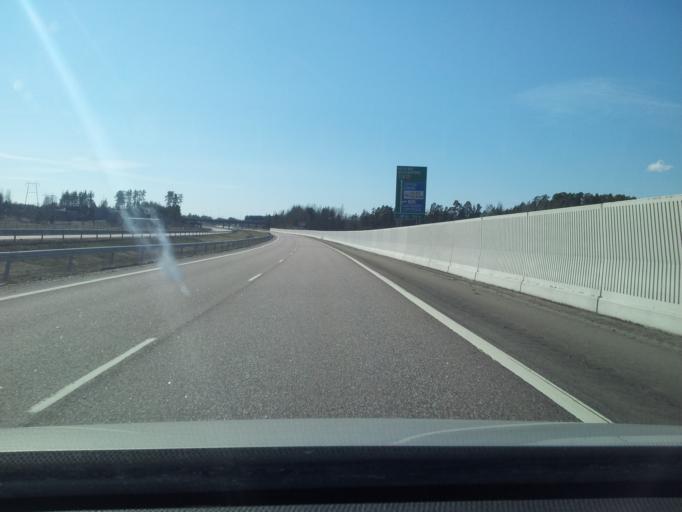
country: FI
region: Uusimaa
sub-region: Loviisa
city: Lovisa
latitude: 60.4664
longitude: 26.2171
